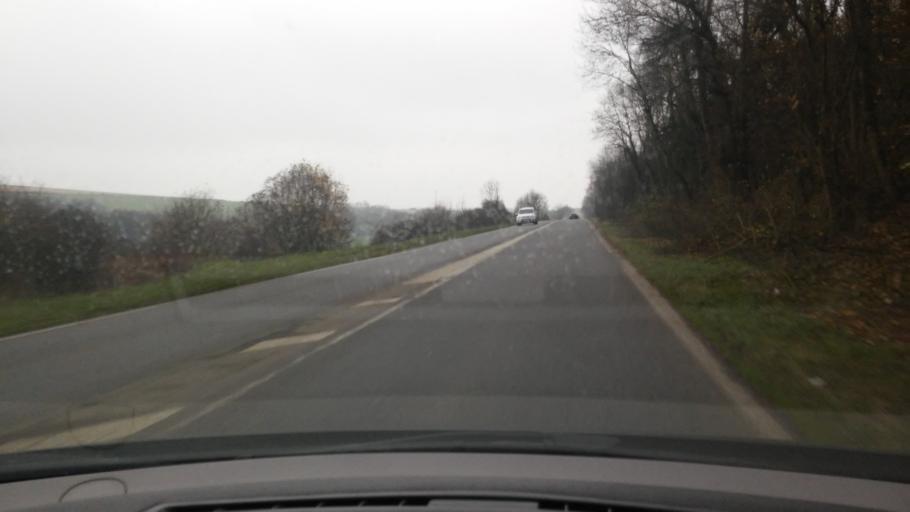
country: FR
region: Lorraine
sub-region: Departement de la Moselle
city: Courcelles-Chaussy
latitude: 49.1031
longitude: 6.4759
